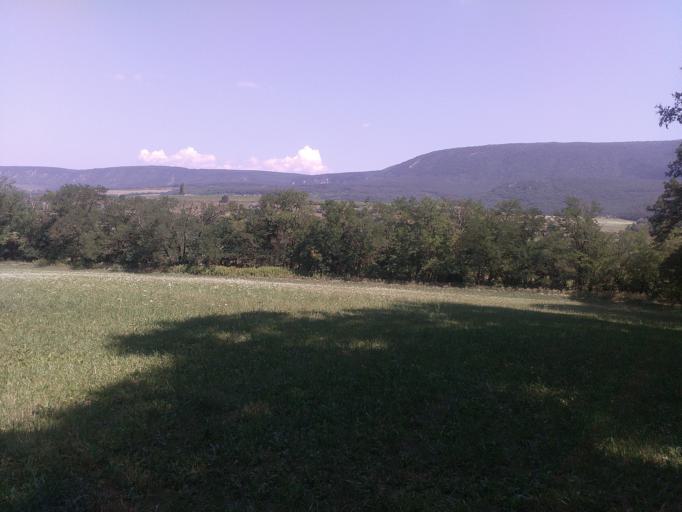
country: HU
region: Komarom-Esztergom
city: Piliscsev
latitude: 47.6687
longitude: 18.8242
